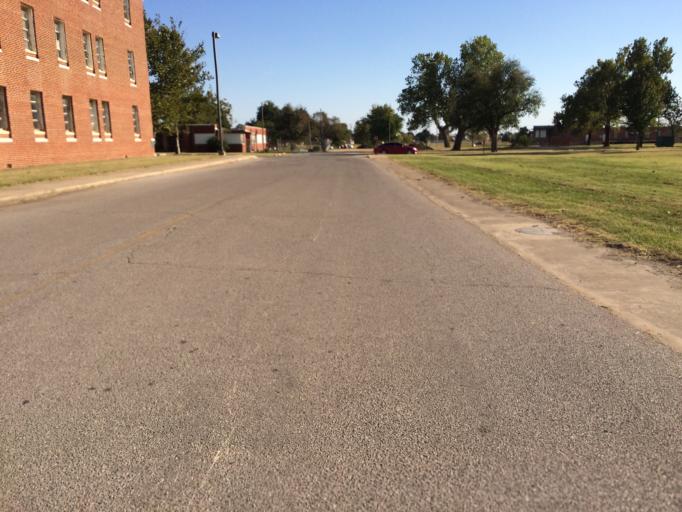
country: US
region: Oklahoma
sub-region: Cleveland County
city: Norman
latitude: 35.2286
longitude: -97.4271
